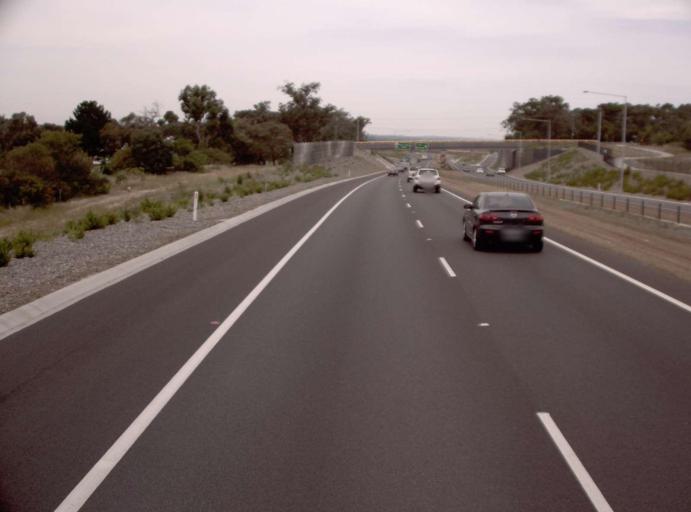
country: AU
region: Victoria
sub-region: Frankston
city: Langwarrin
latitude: -38.1746
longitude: 145.1625
